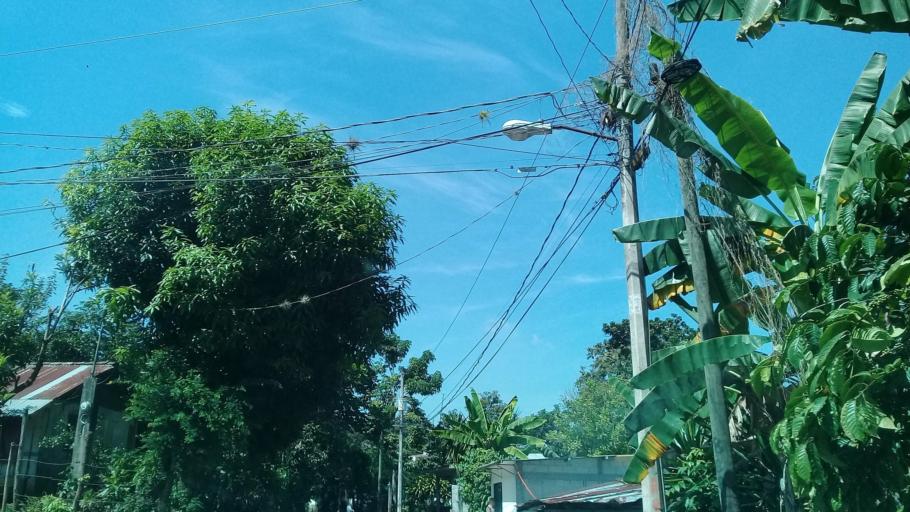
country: MX
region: Veracruz
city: Amatlan de los Reyes
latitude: 18.8416
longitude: -96.9157
